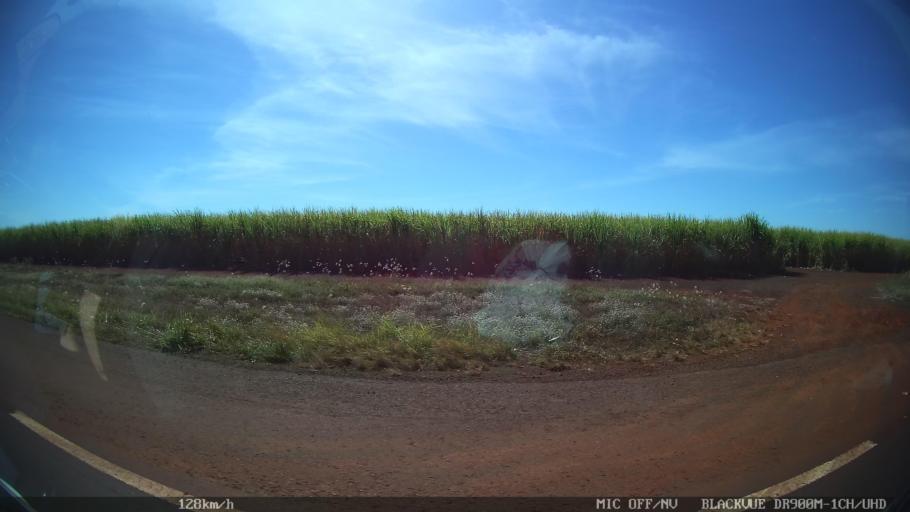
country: BR
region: Sao Paulo
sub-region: Guaira
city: Guaira
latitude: -20.4437
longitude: -48.3127
